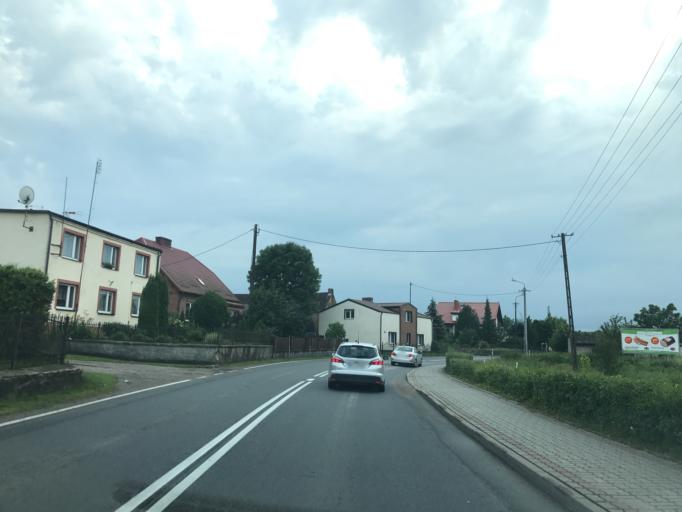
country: PL
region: Pomeranian Voivodeship
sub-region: Powiat czluchowski
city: Rzeczenica
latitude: 53.7552
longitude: 17.1176
